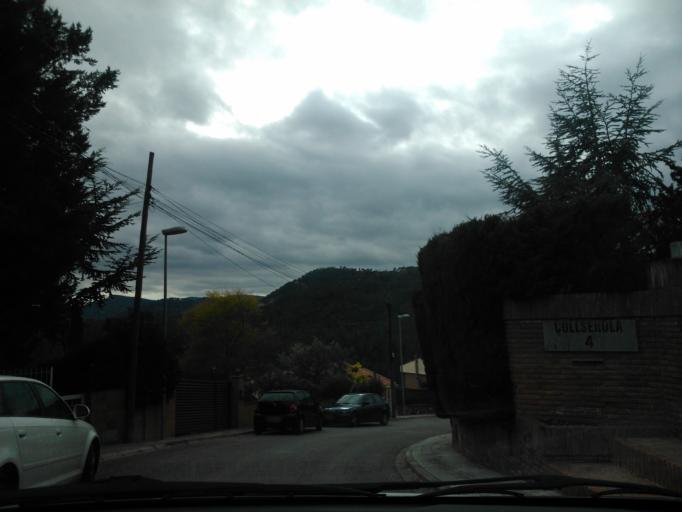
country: ES
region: Catalonia
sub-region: Provincia de Barcelona
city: Cervello
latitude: 41.4158
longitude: 1.9689
